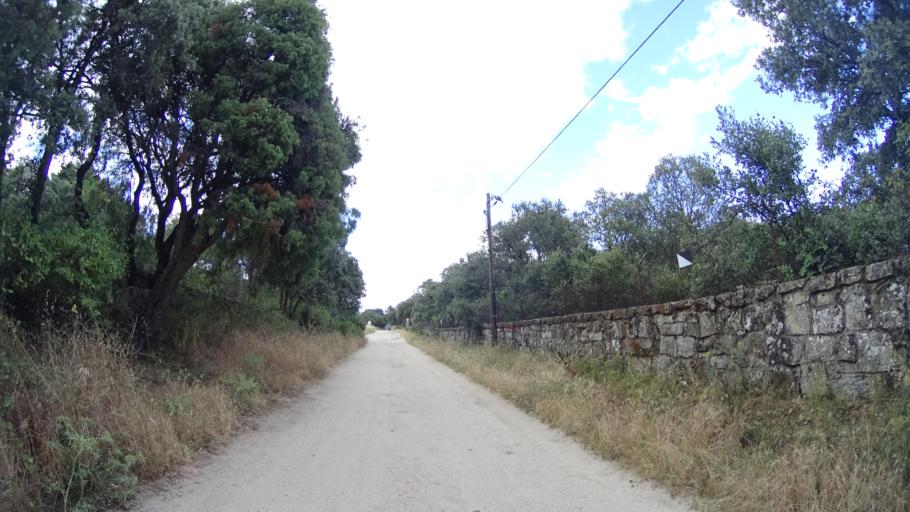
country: ES
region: Madrid
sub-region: Provincia de Madrid
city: Hoyo de Manzanares
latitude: 40.6313
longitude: -3.8971
